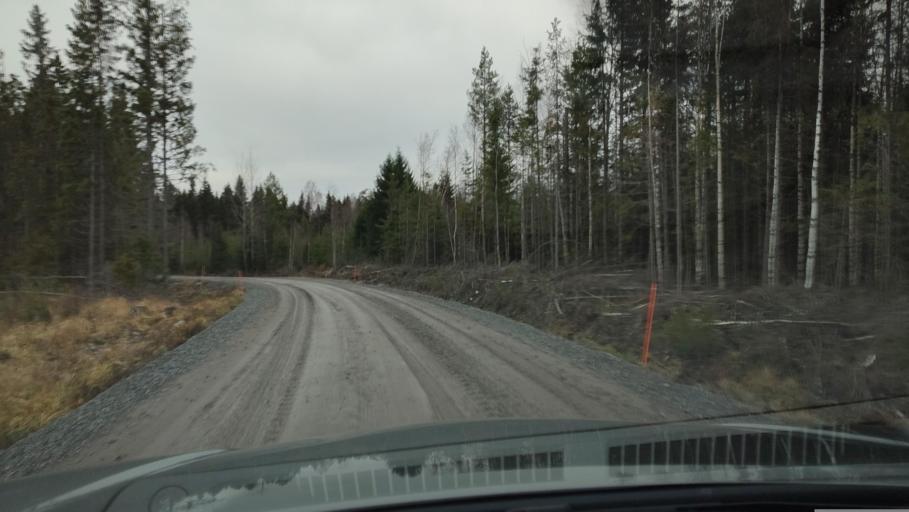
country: FI
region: Southern Ostrobothnia
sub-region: Suupohja
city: Karijoki
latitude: 62.1992
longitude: 21.5743
